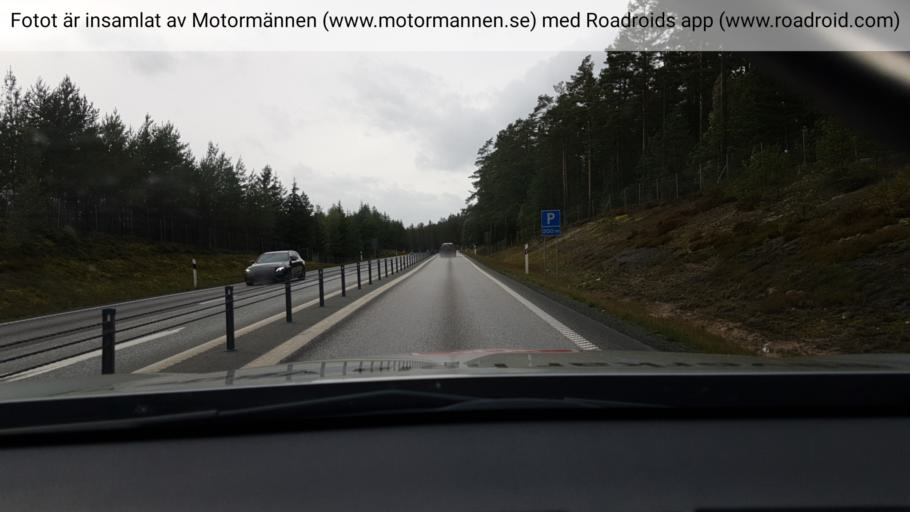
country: SE
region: Joenkoeping
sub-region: Jonkopings Kommun
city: Jonkoping
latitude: 57.7746
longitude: 14.0685
